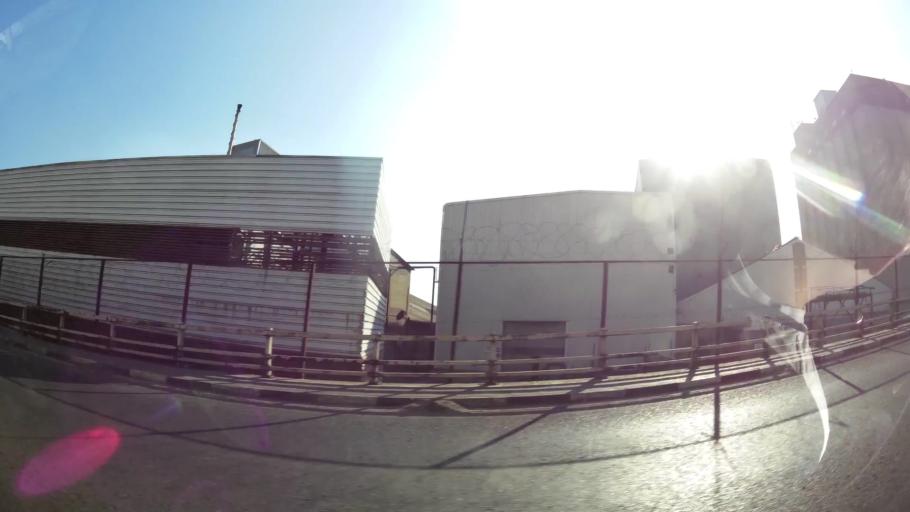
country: ZA
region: Gauteng
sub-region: West Rand District Municipality
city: Randfontein
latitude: -26.1645
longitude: 27.7124
